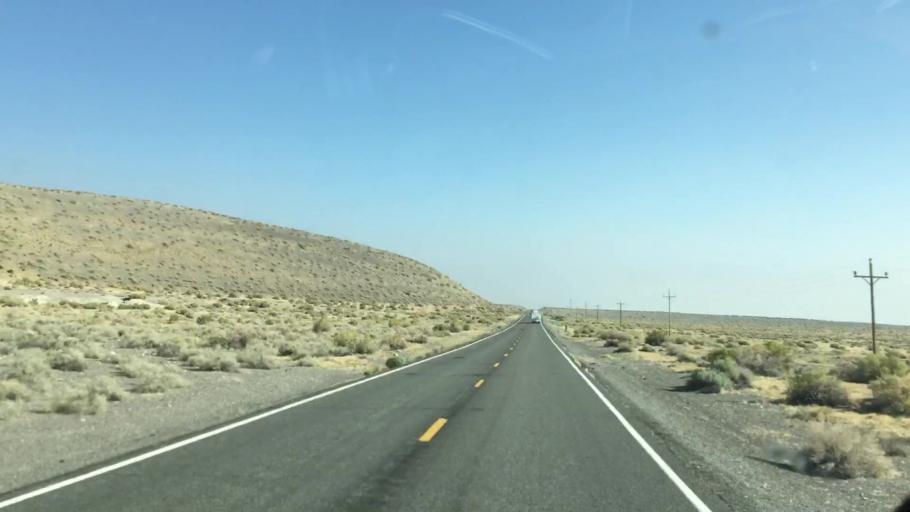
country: US
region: Nevada
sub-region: Lyon County
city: Fernley
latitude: 40.1615
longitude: -119.3684
